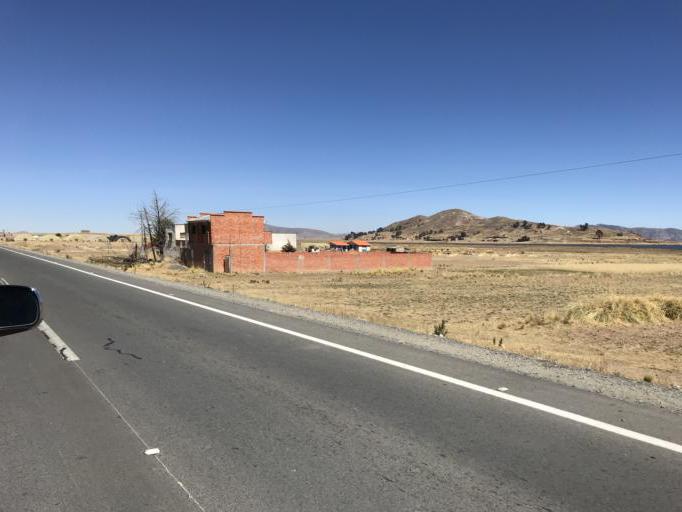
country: BO
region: La Paz
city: Huarina
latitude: -16.2157
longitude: -68.5893
